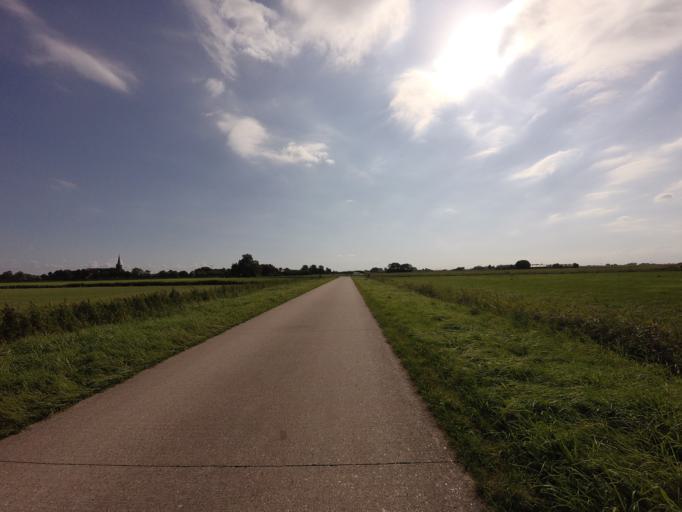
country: NL
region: Friesland
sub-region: Gemeente Littenseradiel
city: Makkum
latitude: 53.0805
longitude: 5.6317
